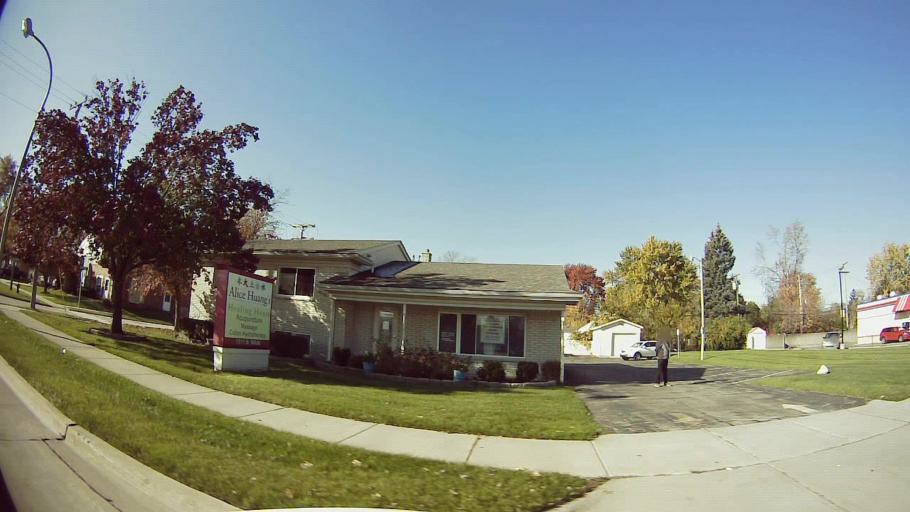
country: US
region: Michigan
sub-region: Oakland County
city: Clawson
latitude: 42.5448
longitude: -83.1469
